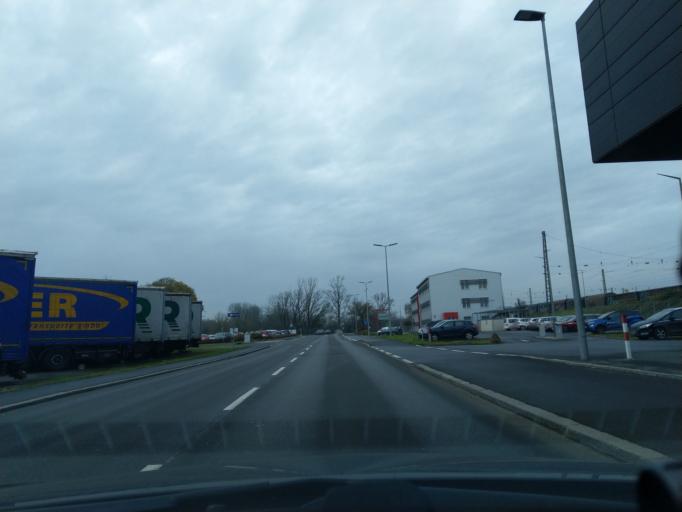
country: AT
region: Upper Austria
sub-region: Politischer Bezirk Urfahr-Umgebung
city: Steyregg
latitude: 48.2625
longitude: 14.3374
